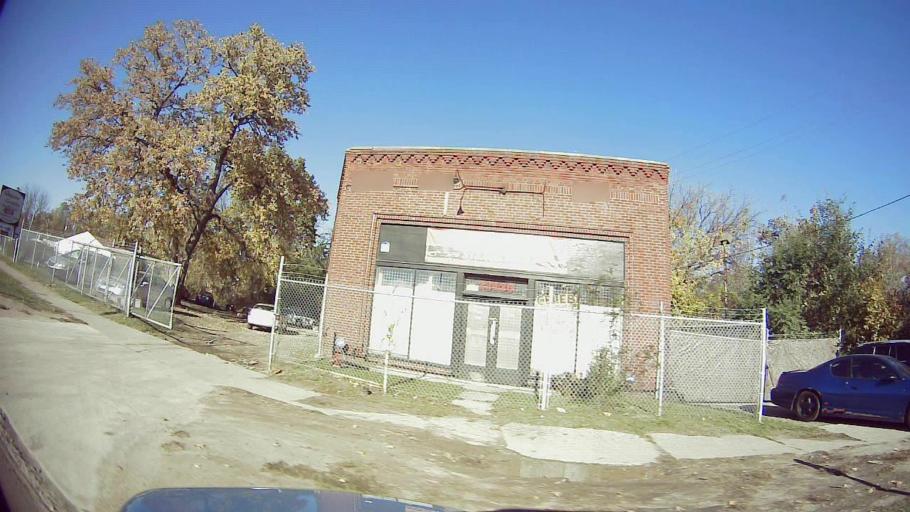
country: US
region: Michigan
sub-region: Wayne County
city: Redford
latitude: 42.4219
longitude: -83.2704
